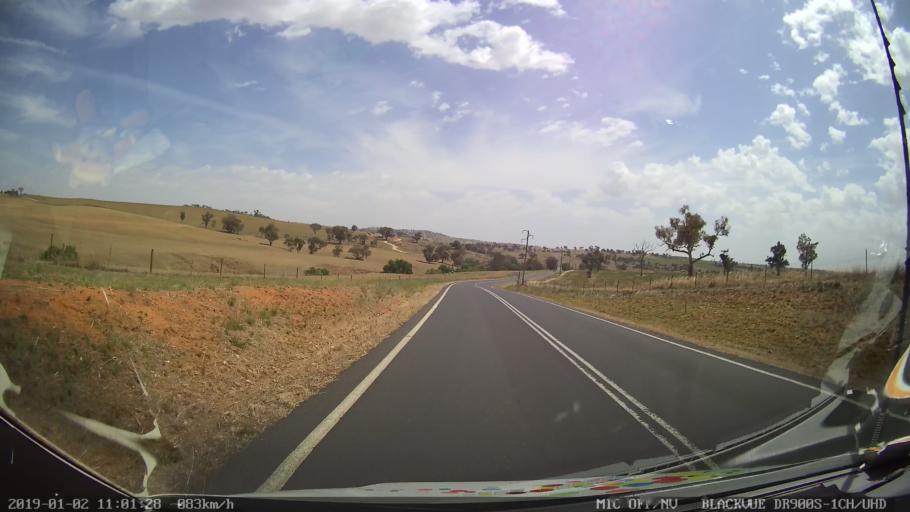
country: AU
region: New South Wales
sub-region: Young
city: Young
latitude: -34.5976
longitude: 148.3203
